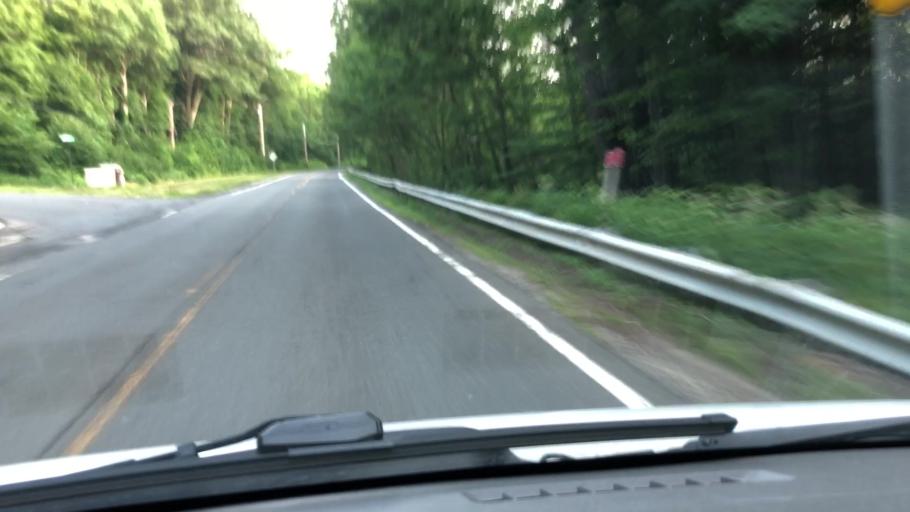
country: US
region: Massachusetts
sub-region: Hampshire County
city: Chesterfield
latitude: 42.4285
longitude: -72.7866
